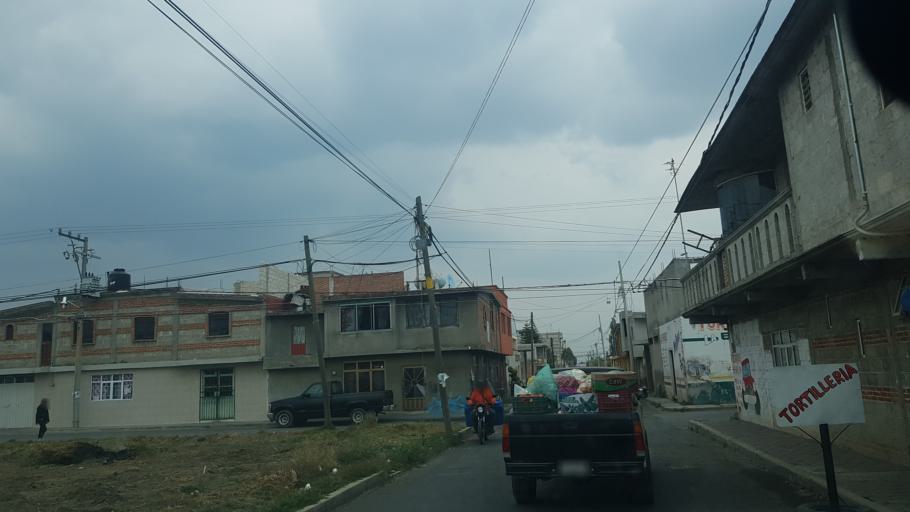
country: MX
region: Puebla
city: Huejotzingo
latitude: 19.1601
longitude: -98.4139
